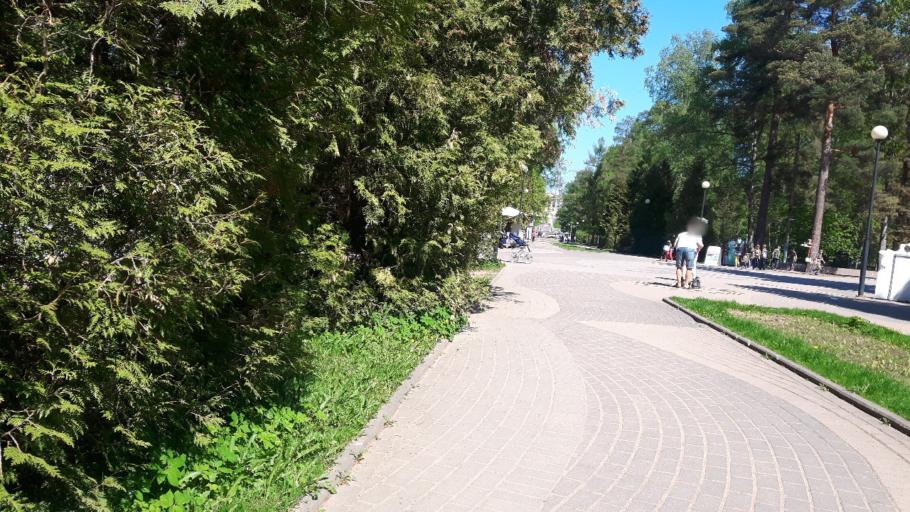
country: RU
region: St.-Petersburg
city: Zelenogorsk
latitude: 60.1894
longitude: 29.7002
